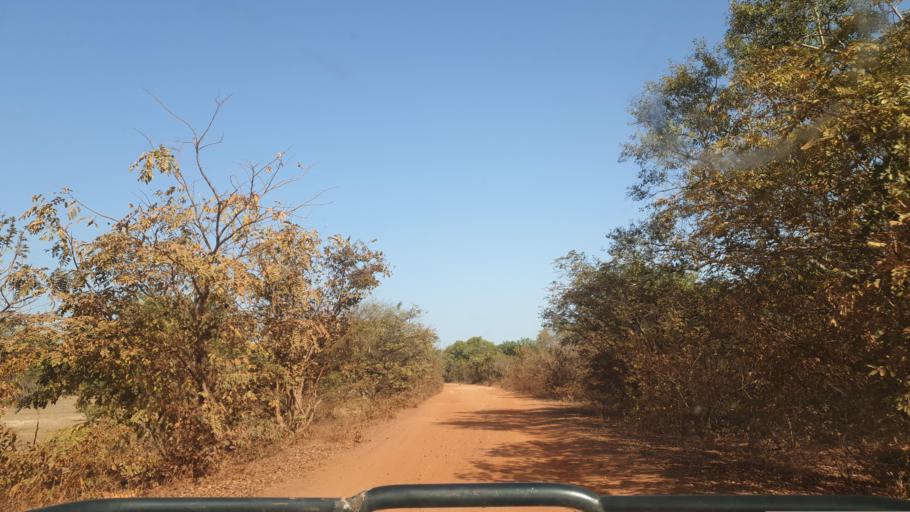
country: ML
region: Sikasso
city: Bougouni
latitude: 11.7821
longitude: -6.9083
